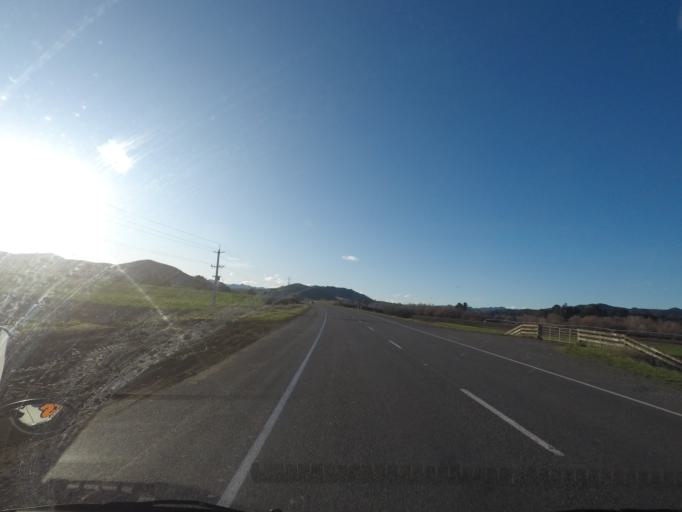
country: NZ
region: Canterbury
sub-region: Kaikoura District
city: Kaikoura
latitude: -42.6987
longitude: 173.3021
